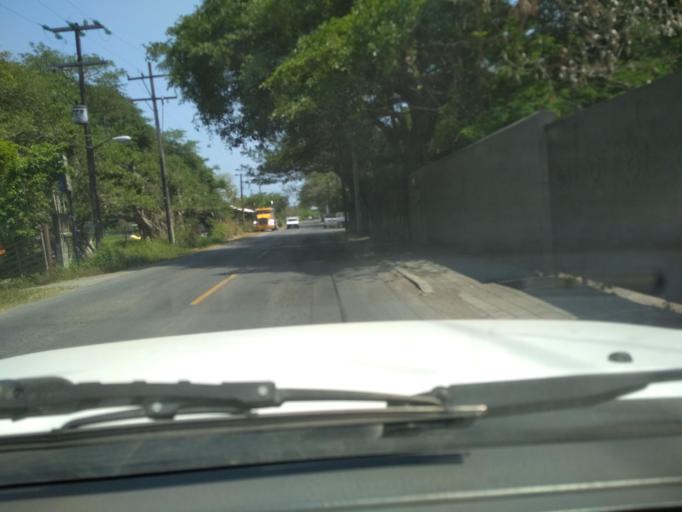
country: MX
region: Veracruz
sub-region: Medellin
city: Fraccionamiento Arboledas San Ramon
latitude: 19.0962
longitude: -96.1382
